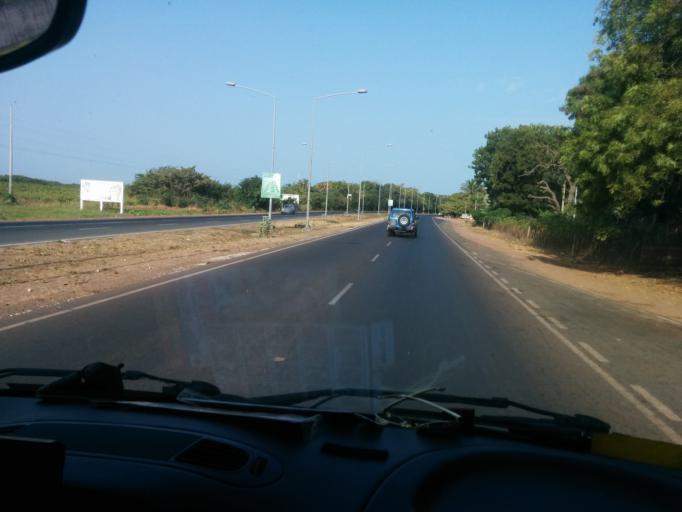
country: GM
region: Banjul
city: Banjul
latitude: 13.4655
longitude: -16.6057
